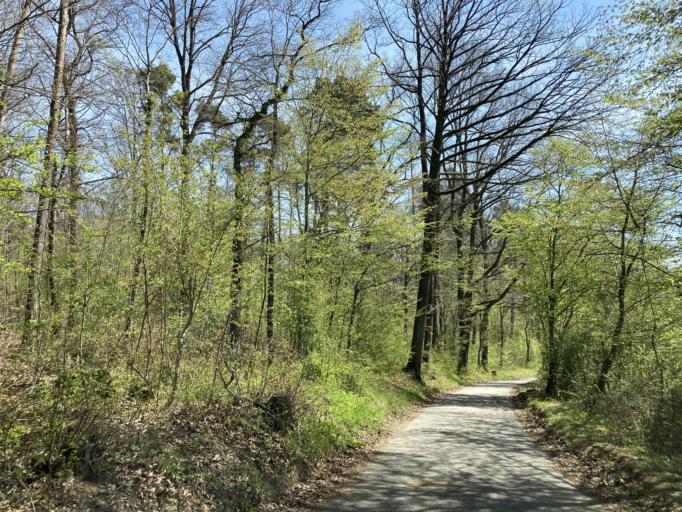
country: DE
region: Baden-Wuerttemberg
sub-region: Tuebingen Region
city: Tuebingen
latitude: 48.5481
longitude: 9.0287
